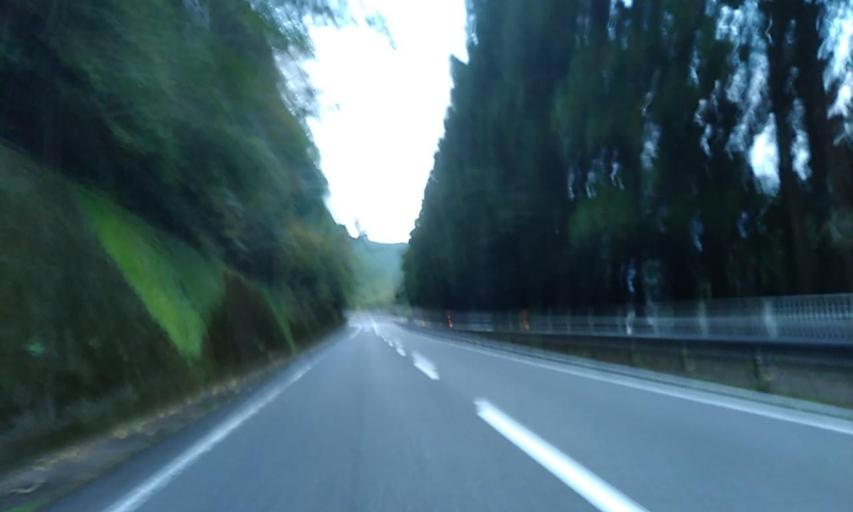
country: JP
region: Wakayama
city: Shingu
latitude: 33.7337
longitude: 135.9421
